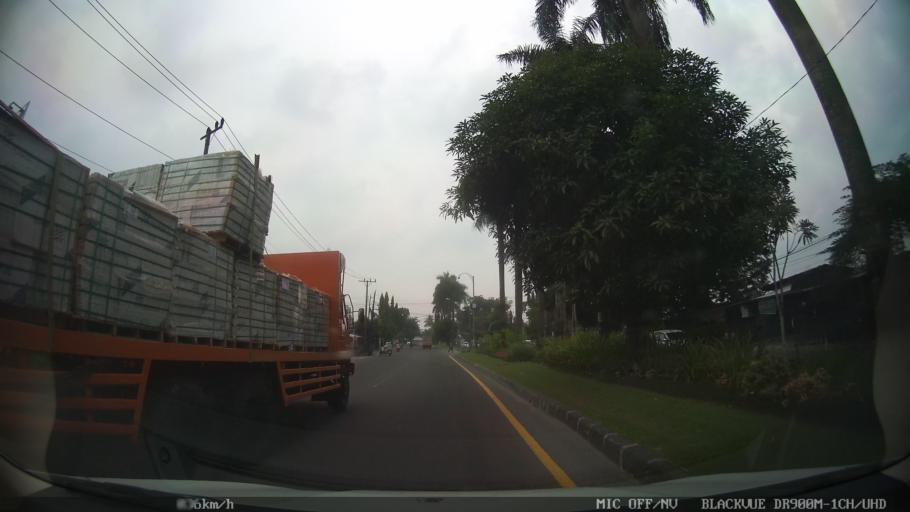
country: ID
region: North Sumatra
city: Deli Tua
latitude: 3.5385
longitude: 98.6979
